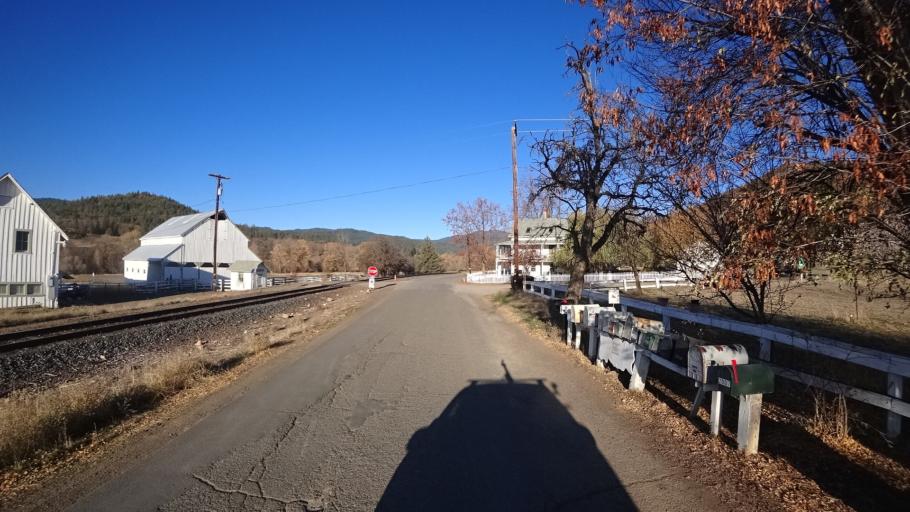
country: US
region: Oregon
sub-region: Jackson County
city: Ashland
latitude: 42.0021
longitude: -122.6406
